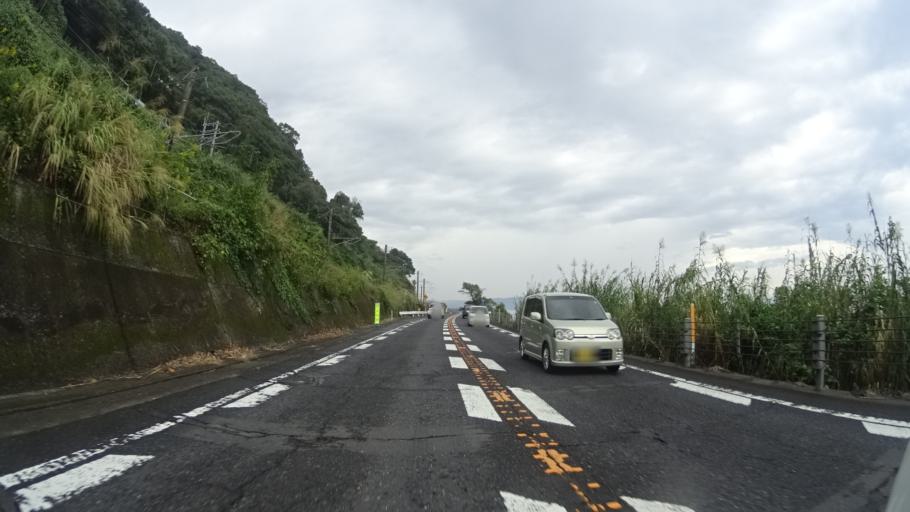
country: JP
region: Kagoshima
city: Kajiki
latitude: 31.6899
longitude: 130.6131
